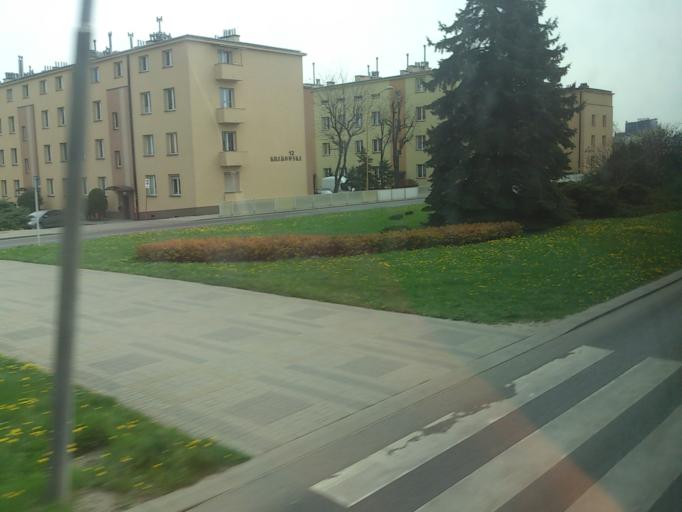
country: PL
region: Subcarpathian Voivodeship
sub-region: Rzeszow
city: Rzeszow
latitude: 50.0452
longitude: 21.9829
